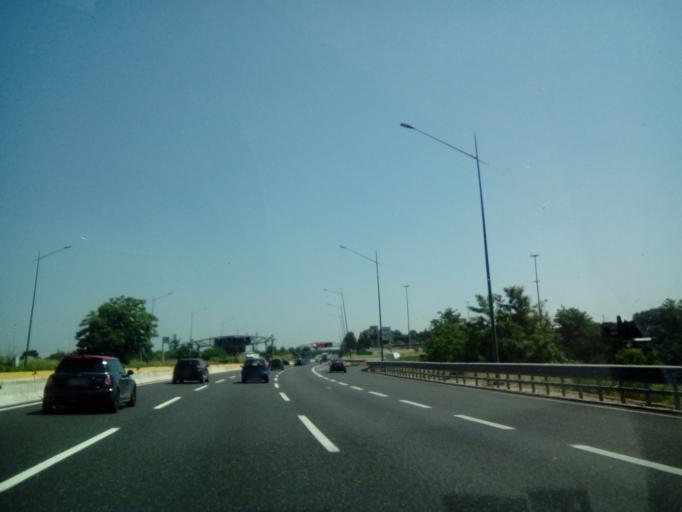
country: IT
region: Latium
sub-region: Citta metropolitana di Roma Capitale
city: Valle Santa
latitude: 41.9574
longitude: 12.3858
